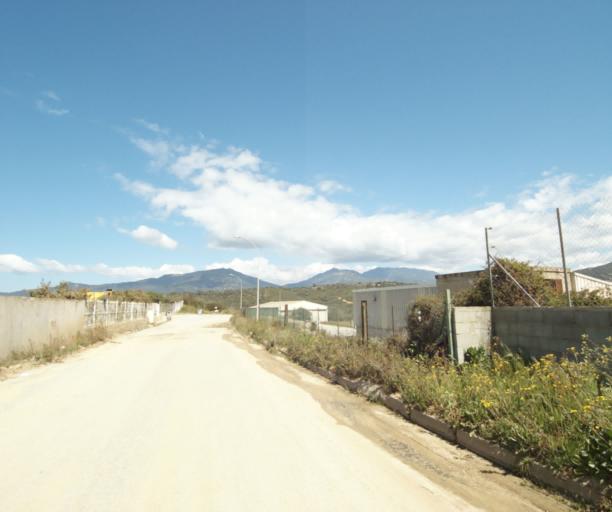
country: FR
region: Corsica
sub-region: Departement de la Corse-du-Sud
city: Propriano
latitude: 41.6555
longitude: 8.8992
